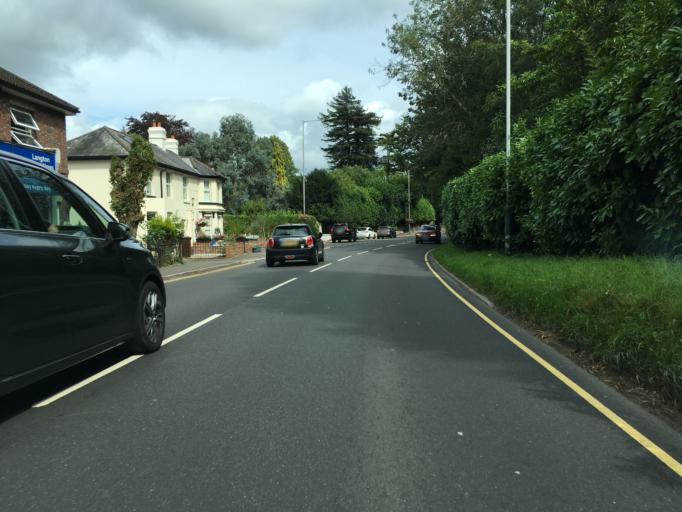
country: GB
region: England
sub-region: Kent
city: Royal Tunbridge Wells
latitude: 51.1309
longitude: 0.2110
